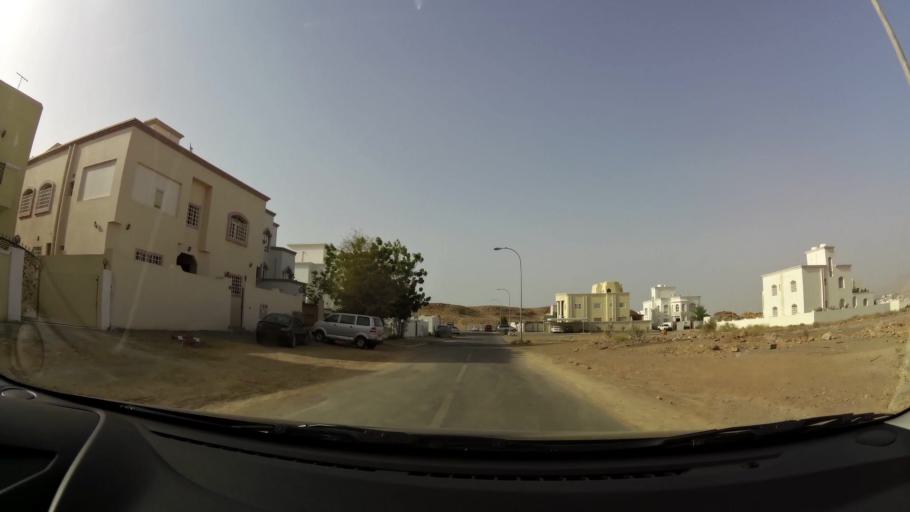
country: OM
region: Muhafazat Masqat
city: Bawshar
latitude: 23.5509
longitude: 58.3635
